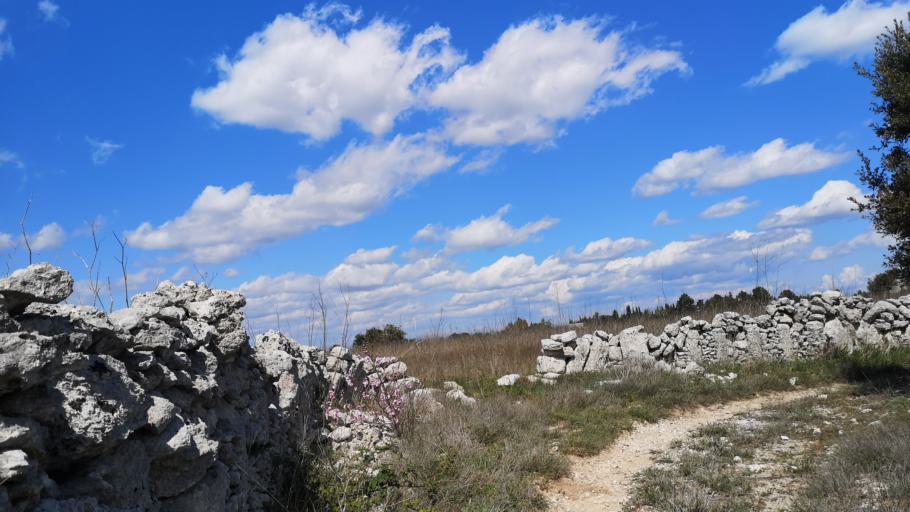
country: IT
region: Apulia
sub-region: Provincia di Lecce
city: Spongano
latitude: 40.0294
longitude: 18.3608
